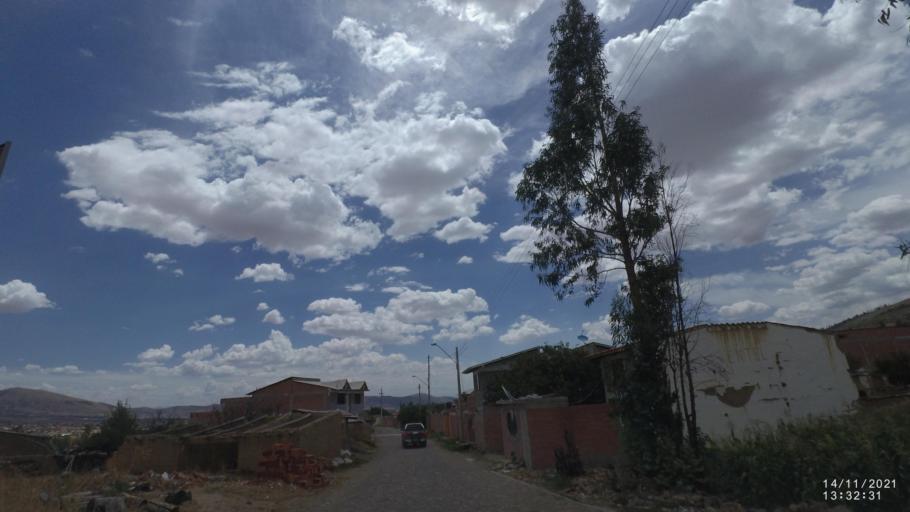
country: BO
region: Cochabamba
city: Colomi
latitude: -17.3969
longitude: -65.9837
